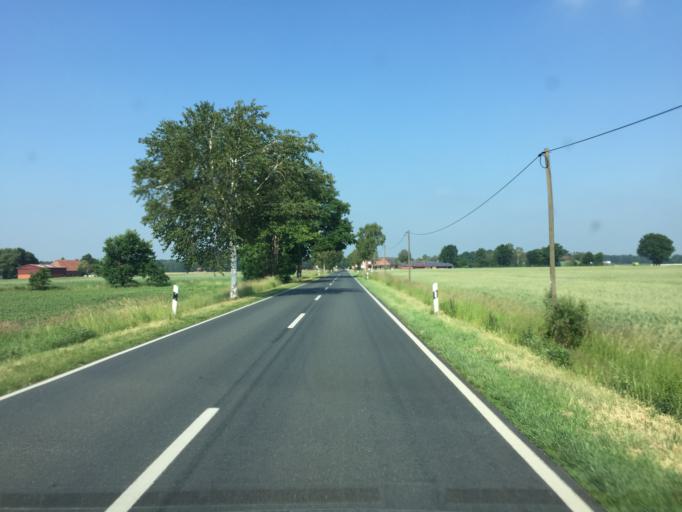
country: DE
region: Lower Saxony
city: Varrel
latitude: 52.5365
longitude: 8.7290
